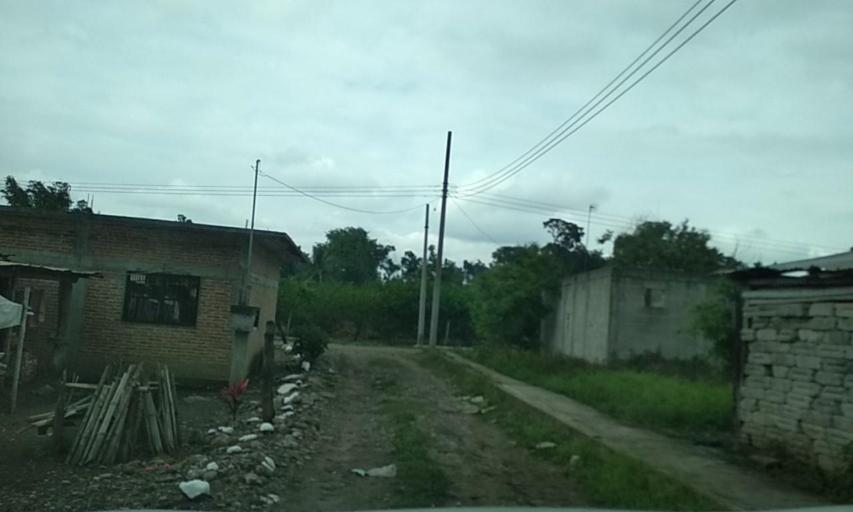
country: MX
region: Veracruz
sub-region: Papantla
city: El Chote
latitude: 20.3642
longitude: -97.4294
